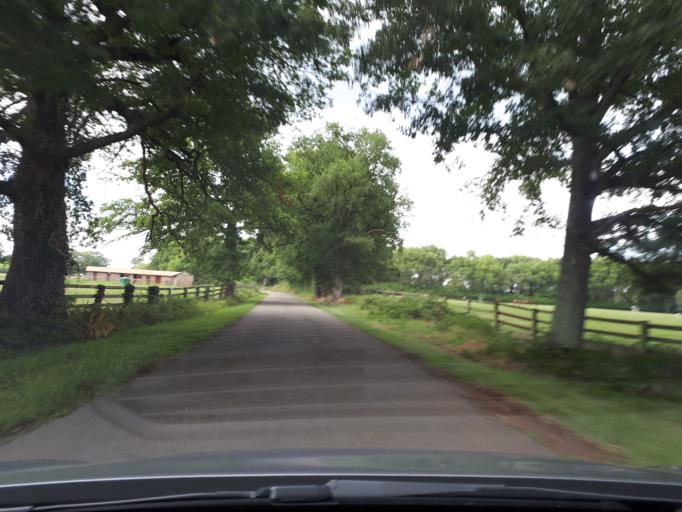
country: FR
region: Pays de la Loire
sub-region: Departement de la Sarthe
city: Champagne
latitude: 48.0677
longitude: 0.3044
